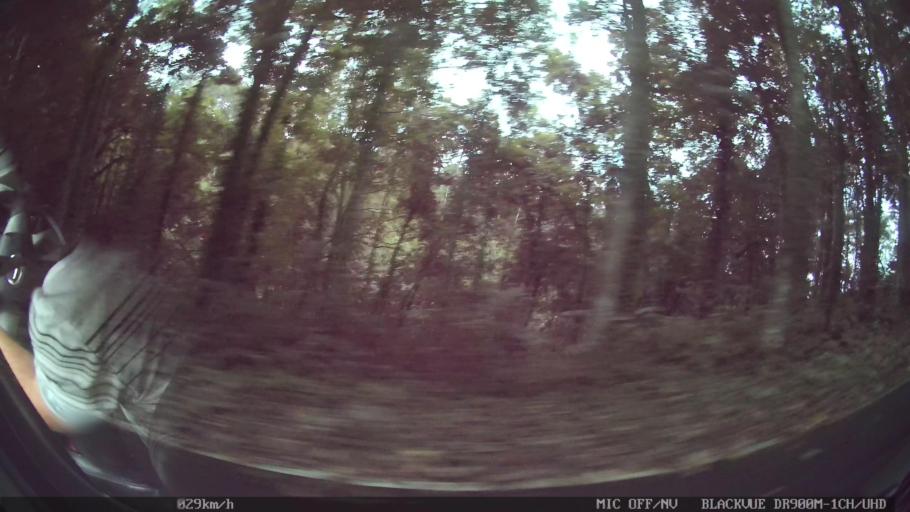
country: ID
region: Bali
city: Petang
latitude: -8.3677
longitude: 115.2219
